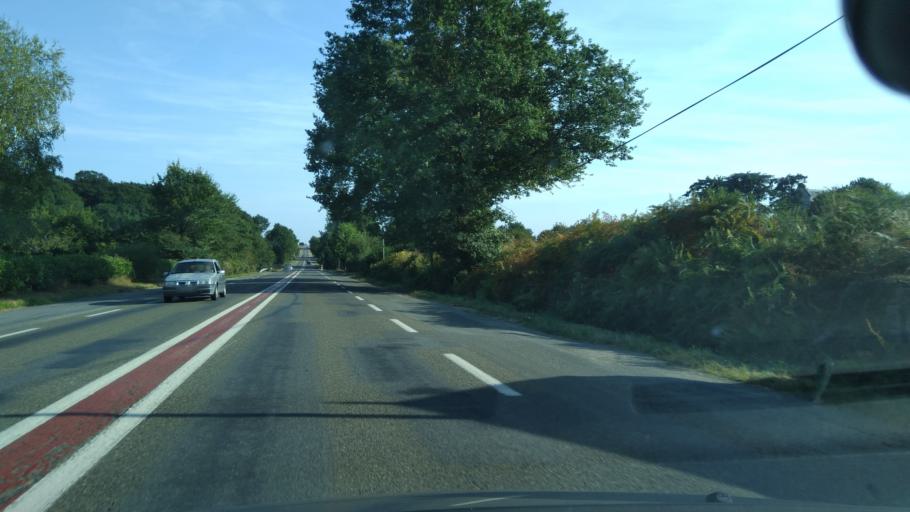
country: FR
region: Pays de la Loire
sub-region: Departement de la Mayenne
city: Entrammes
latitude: 48.0249
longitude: -0.7346
